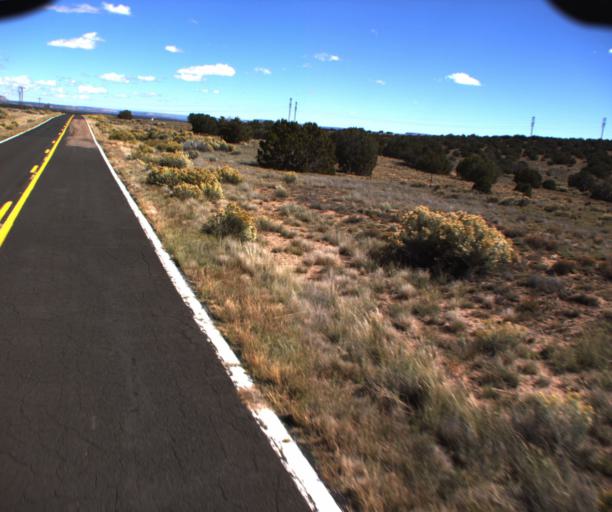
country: US
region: New Mexico
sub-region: McKinley County
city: Zuni Pueblo
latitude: 35.0169
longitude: -109.0535
